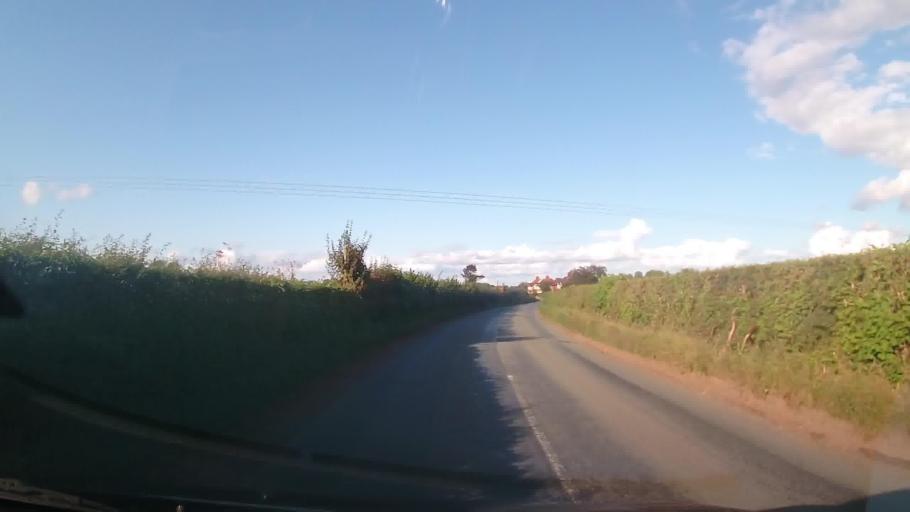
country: GB
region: England
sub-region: Shropshire
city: Great Hanwood
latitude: 52.6562
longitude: -2.8227
